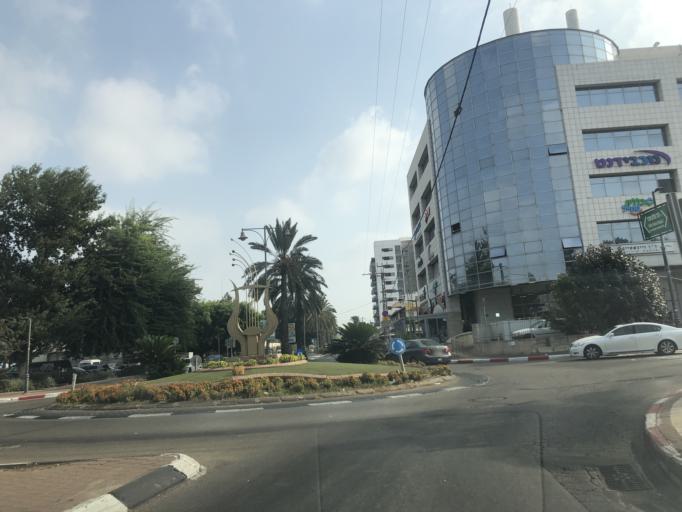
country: IL
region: Central District
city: Rosh Ha'Ayin
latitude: 32.0972
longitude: 34.9430
